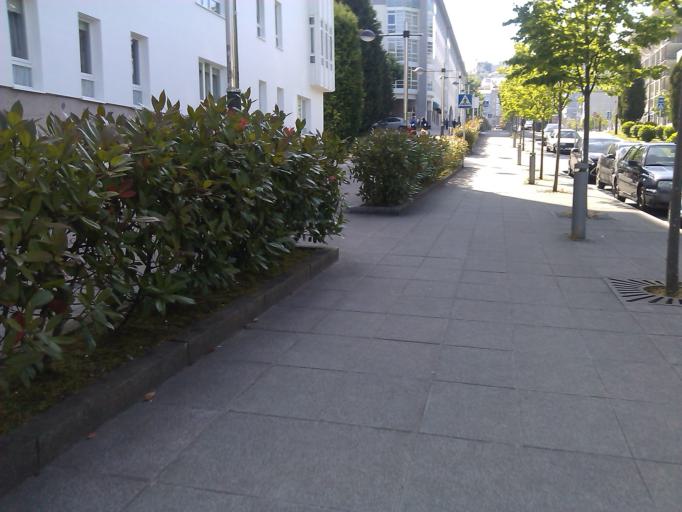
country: ES
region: Galicia
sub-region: Provincia da Coruna
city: Santiago de Compostela
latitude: 42.8833
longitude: -8.5301
